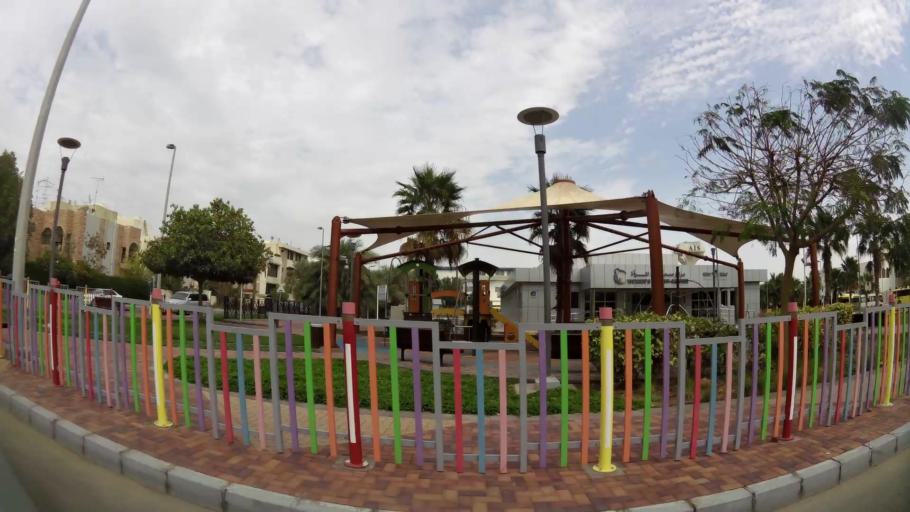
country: AE
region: Abu Dhabi
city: Abu Dhabi
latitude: 24.4617
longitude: 54.3645
